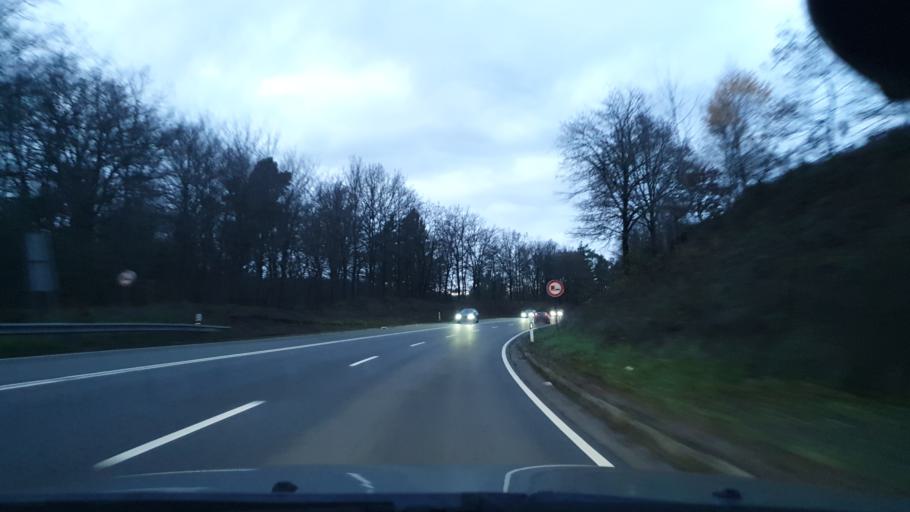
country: DE
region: Rheinland-Pfalz
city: Schopp
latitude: 49.3336
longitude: 7.6717
